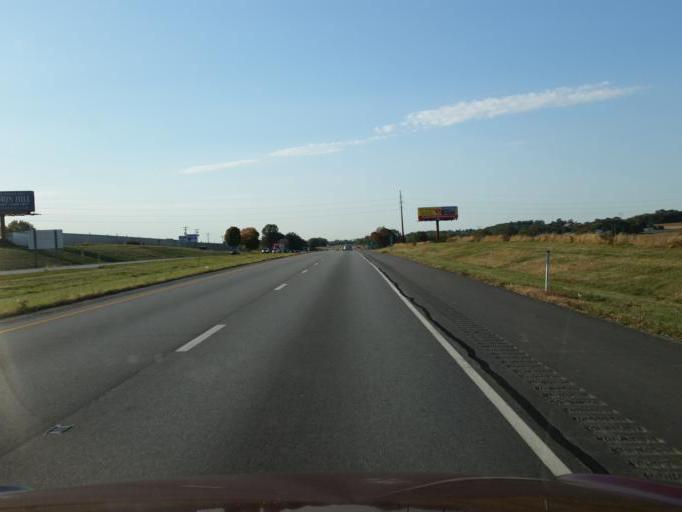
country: US
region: Pennsylvania
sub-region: Lancaster County
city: Salunga
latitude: 40.1203
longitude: -76.4603
